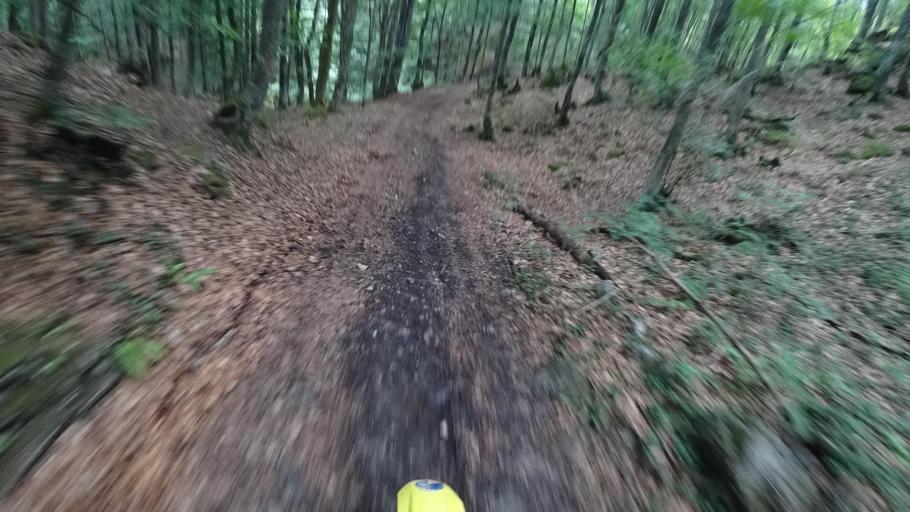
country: HR
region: Karlovacka
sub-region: Grad Ogulin
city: Ogulin
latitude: 45.2293
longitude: 15.1810
